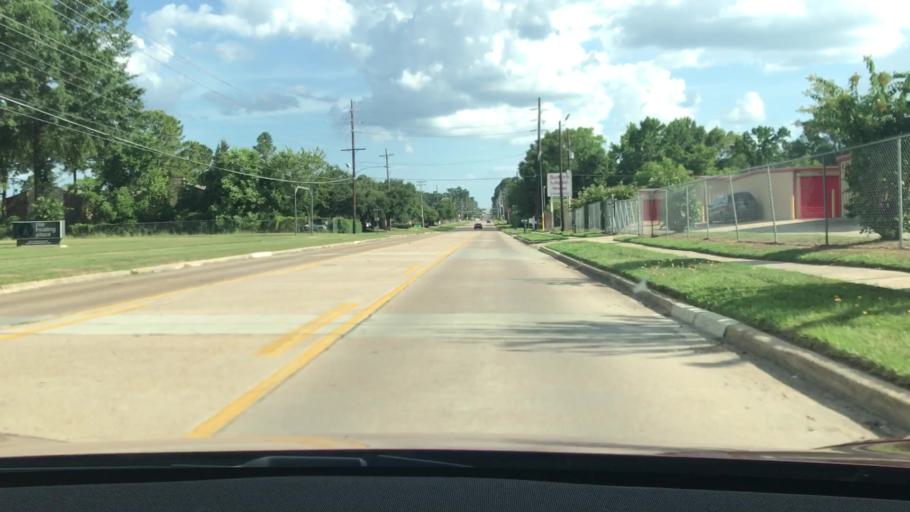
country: US
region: Louisiana
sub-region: Bossier Parish
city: Bossier City
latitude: 32.4065
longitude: -93.7804
